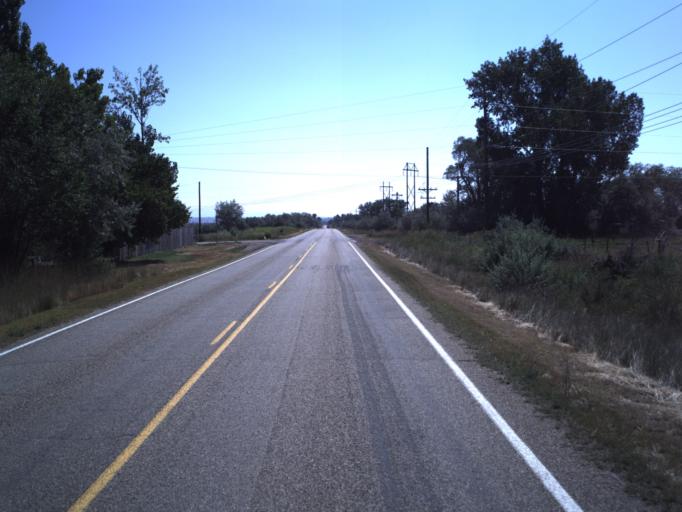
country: US
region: Utah
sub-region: Duchesne County
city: Roosevelt
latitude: 40.2580
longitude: -110.1444
